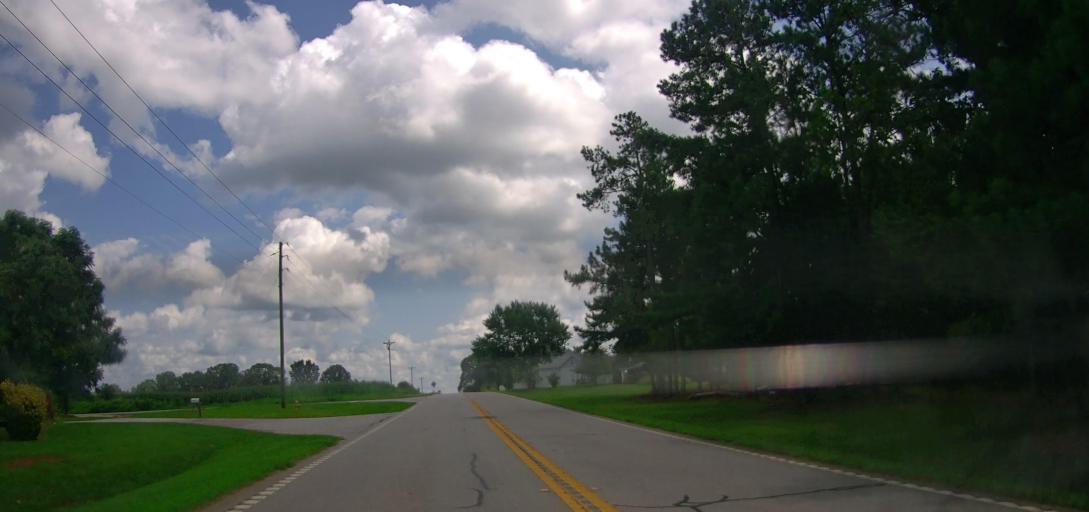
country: US
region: Georgia
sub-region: Heard County
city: Franklin
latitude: 33.3552
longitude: -85.1935
